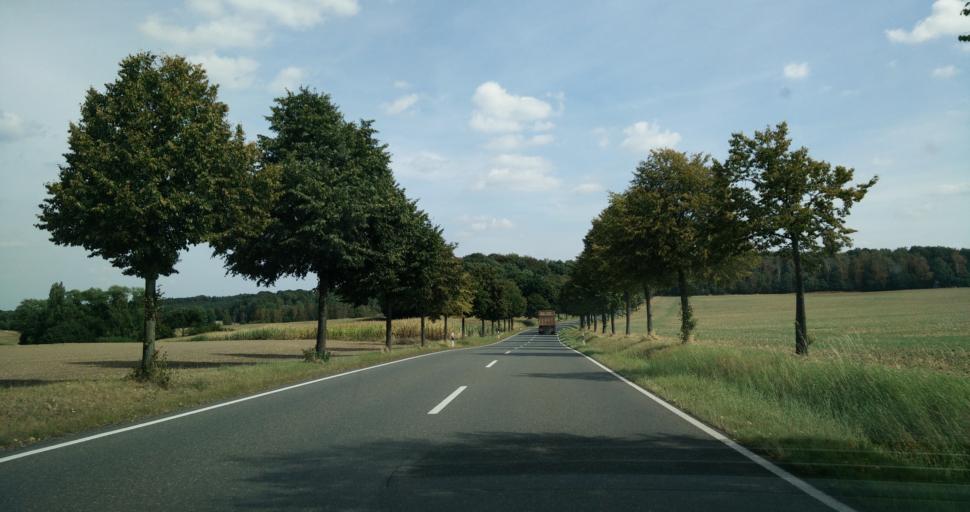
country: DE
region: Saxony
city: Bad Lausick
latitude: 51.1339
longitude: 12.7030
